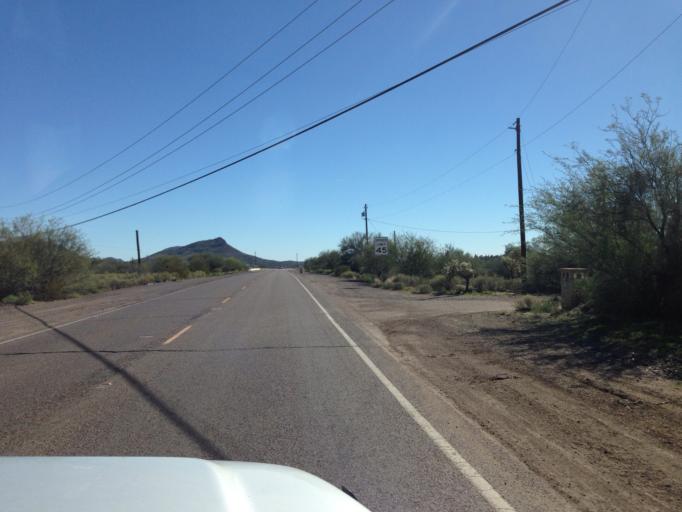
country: US
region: Arizona
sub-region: Maricopa County
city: New River
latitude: 33.9099
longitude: -112.0856
